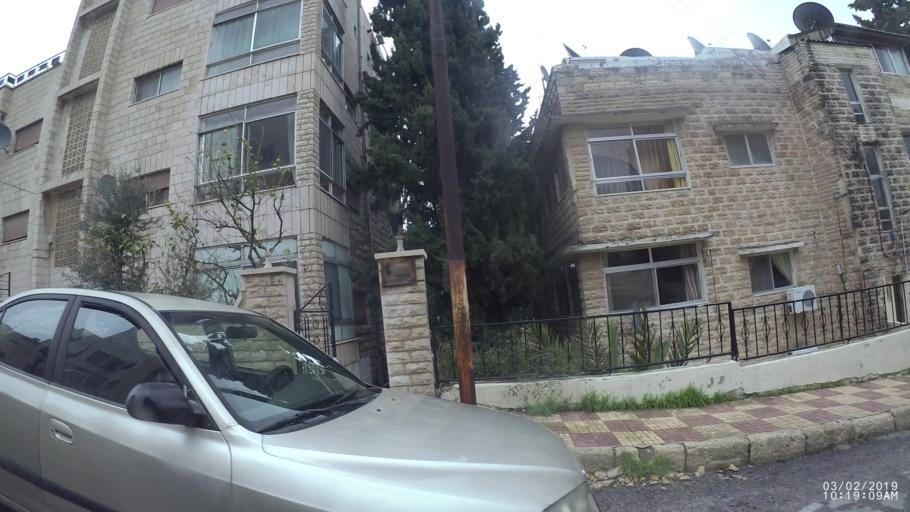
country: JO
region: Amman
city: Amman
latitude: 31.9503
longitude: 35.9105
